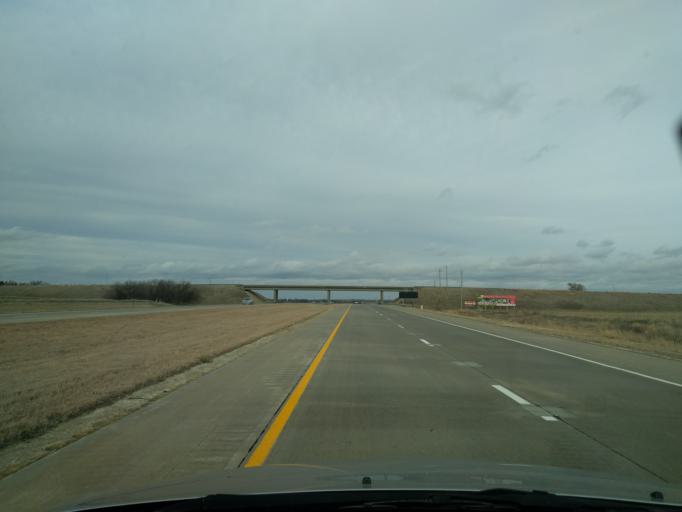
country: US
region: Kansas
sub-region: Saline County
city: Salina
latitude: 38.7087
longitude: -97.6218
